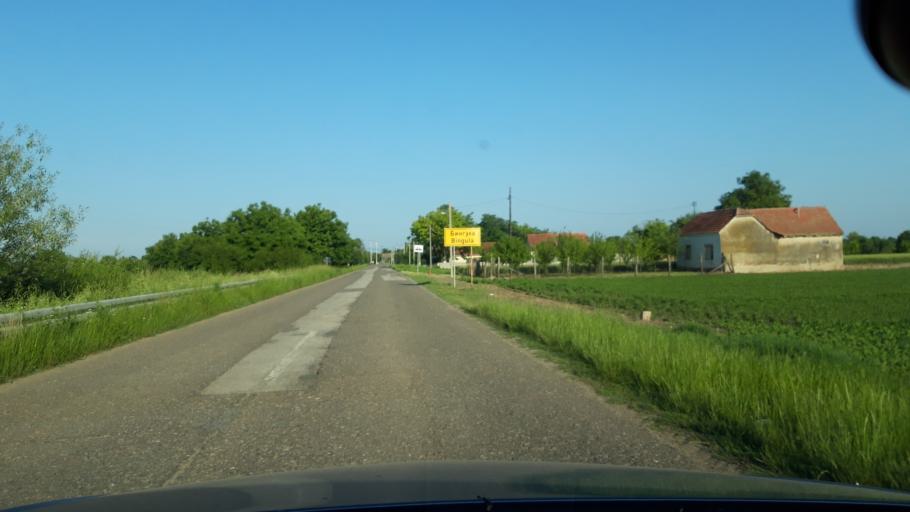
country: HR
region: Vukovarsko-Srijemska
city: Ilok
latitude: 45.1033
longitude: 19.4403
